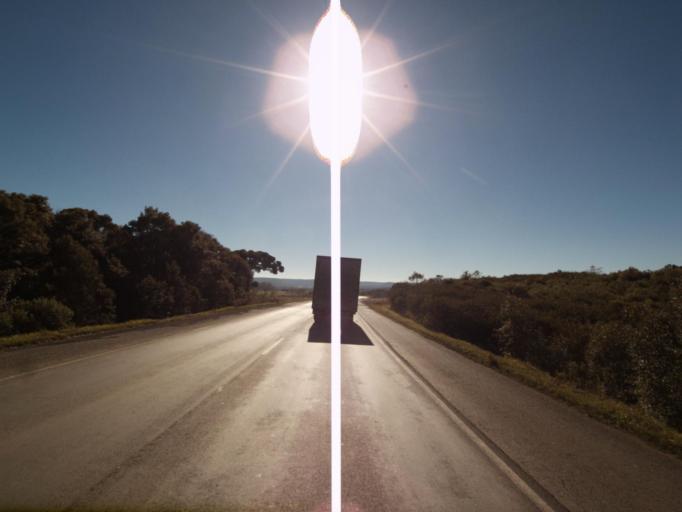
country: BR
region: Santa Catarina
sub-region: Concordia
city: Concordia
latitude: -26.9503
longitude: -51.8287
